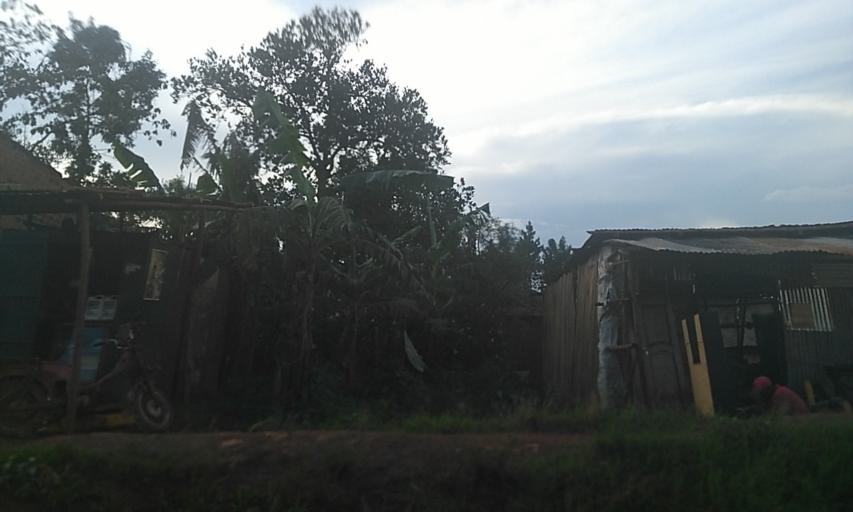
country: UG
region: Central Region
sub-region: Wakiso District
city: Kajansi
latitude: 0.2526
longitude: 32.5051
